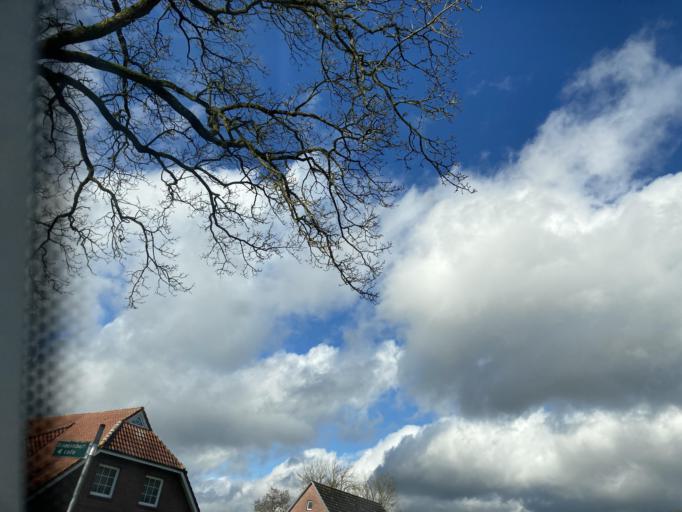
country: DE
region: Lower Saxony
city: Wiesmoor
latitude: 53.3375
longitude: 7.7826
